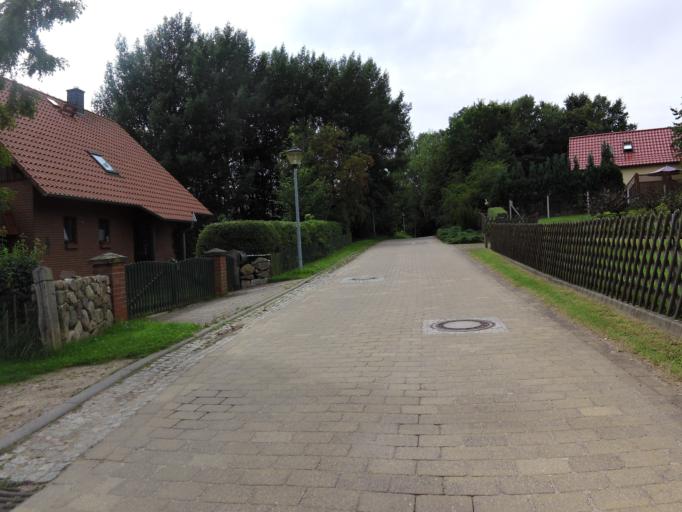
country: DE
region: Mecklenburg-Vorpommern
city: Loitz
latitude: 53.3409
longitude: 13.4293
